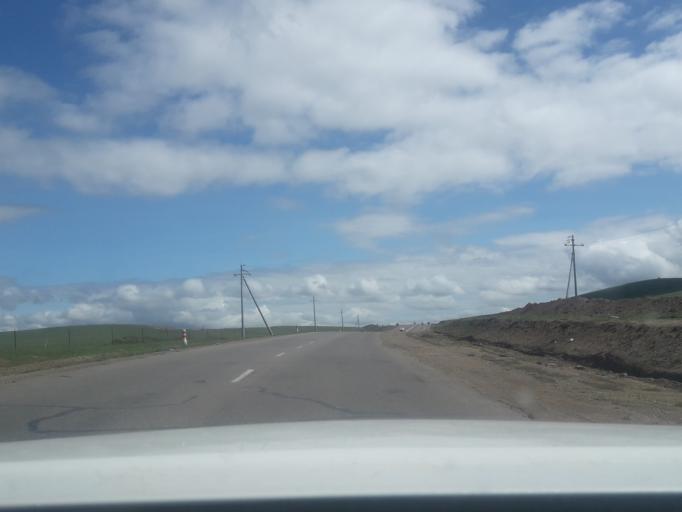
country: MN
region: Central Aimak
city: Altanbulag
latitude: 47.9012
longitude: 106.4934
